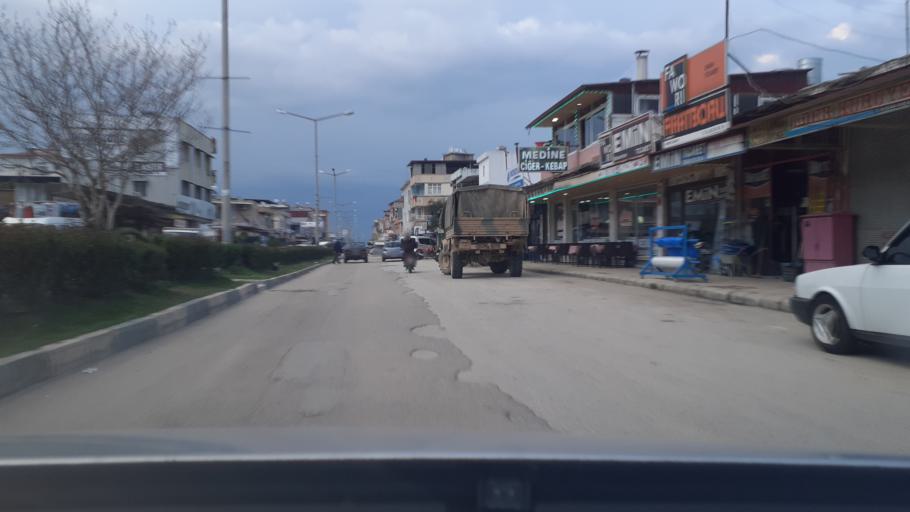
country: TR
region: Hatay
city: Kirikhan
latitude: 36.4960
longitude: 36.3602
